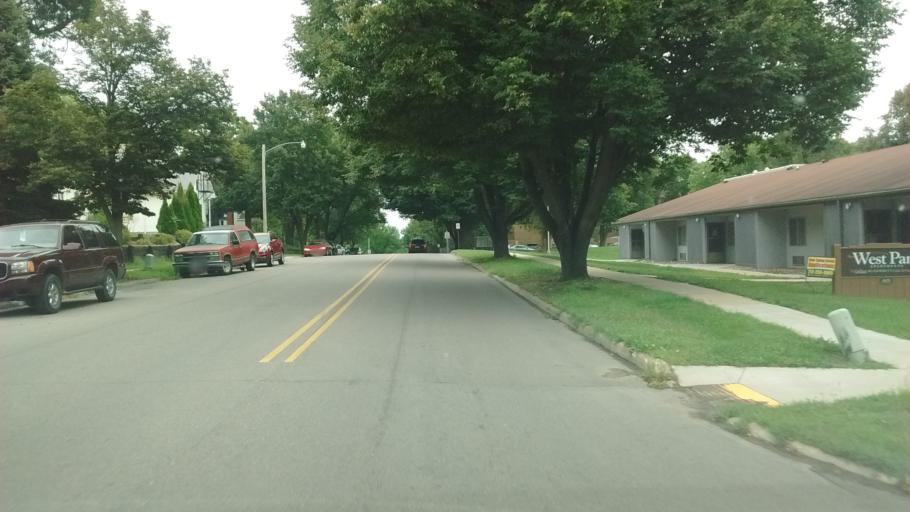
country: US
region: Iowa
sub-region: Woodbury County
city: Sioux City
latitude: 42.4993
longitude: -96.4184
